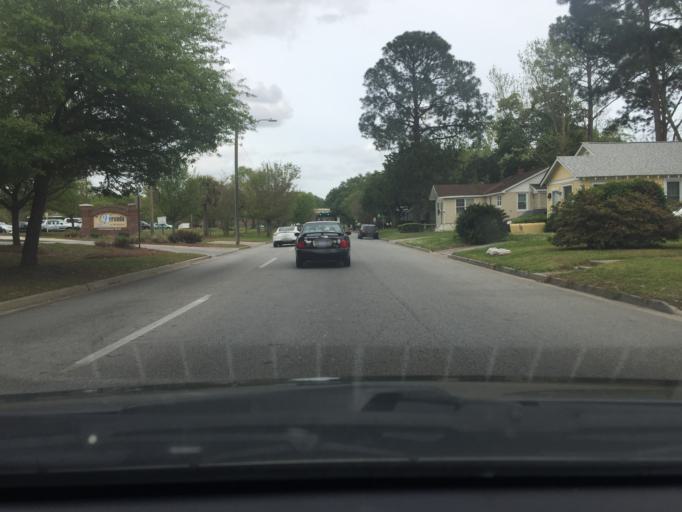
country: US
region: Georgia
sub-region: Chatham County
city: Thunderbolt
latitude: 32.0565
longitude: -81.0760
